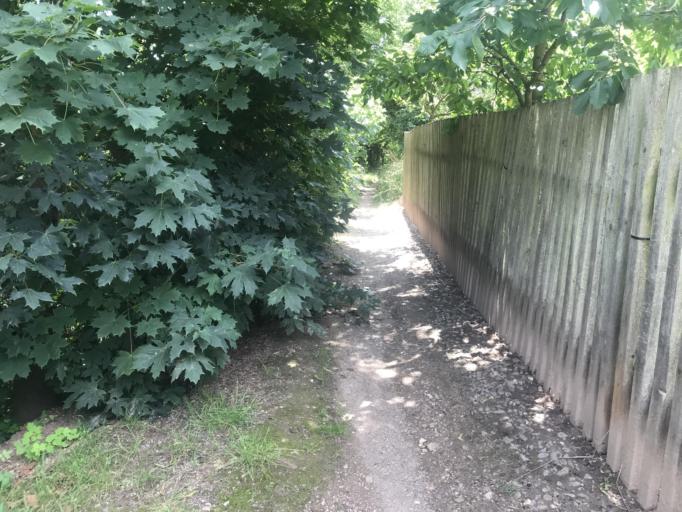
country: DE
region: Saxony-Anhalt
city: Aschersleben
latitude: 51.7331
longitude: 11.4349
